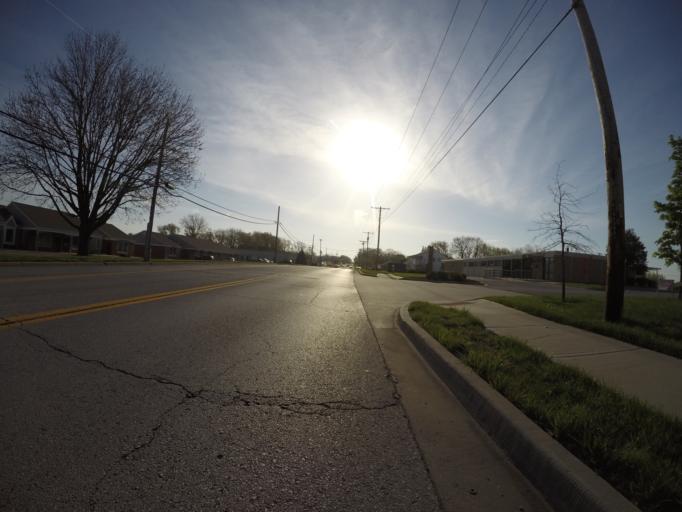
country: US
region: Missouri
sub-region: Jackson County
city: Lees Summit
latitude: 38.9111
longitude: -94.3912
